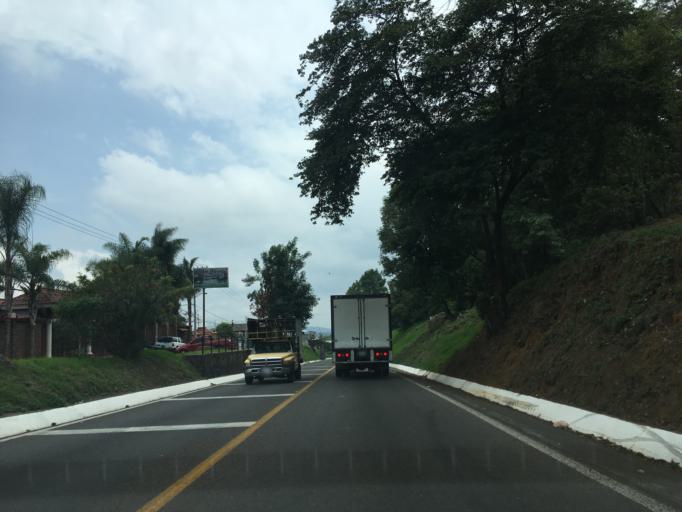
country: MX
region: Michoacan
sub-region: Uruapan
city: Toreo Bajo (El Toreo Bajo)
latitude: 19.4450
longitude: -102.0082
